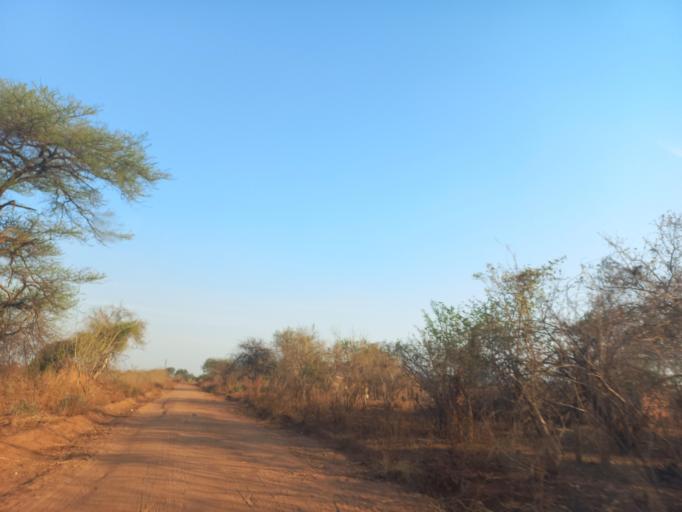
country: ZM
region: Lusaka
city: Luangwa
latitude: -15.4401
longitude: 30.3594
